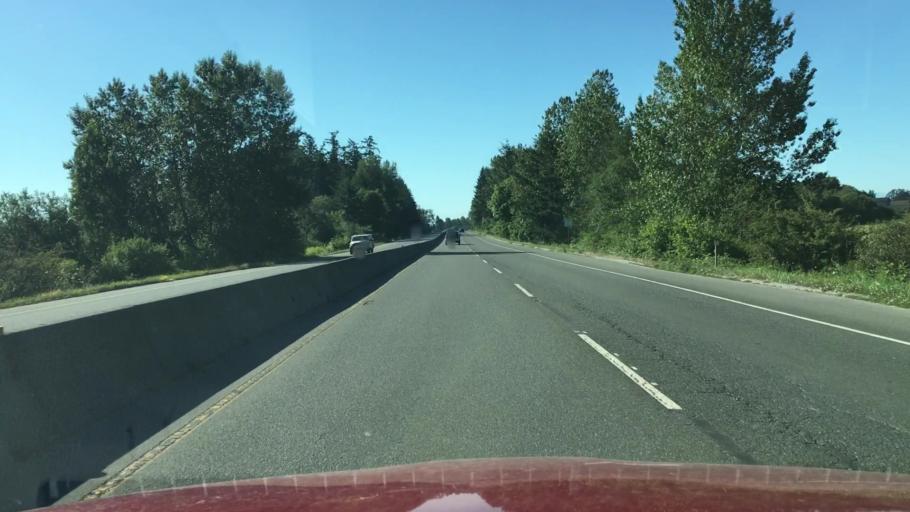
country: CA
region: British Columbia
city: North Saanich
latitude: 48.6705
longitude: -123.4263
